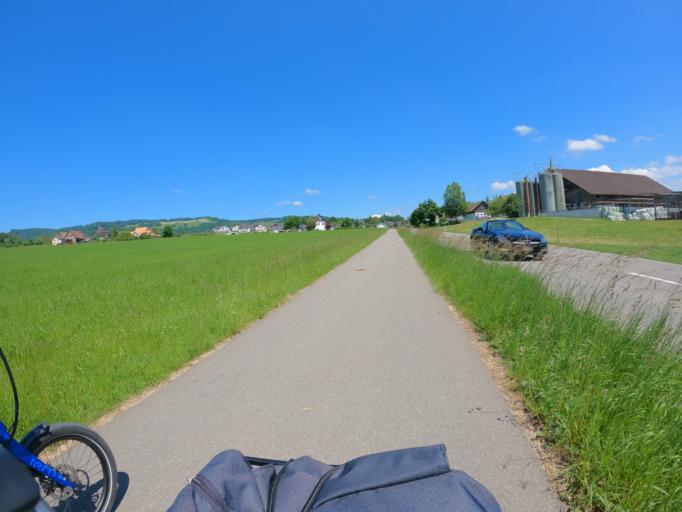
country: CH
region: Zurich
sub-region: Bezirk Affoltern
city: Hausen am Albis / Hausen (Dorf)
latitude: 47.2284
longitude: 8.5220
